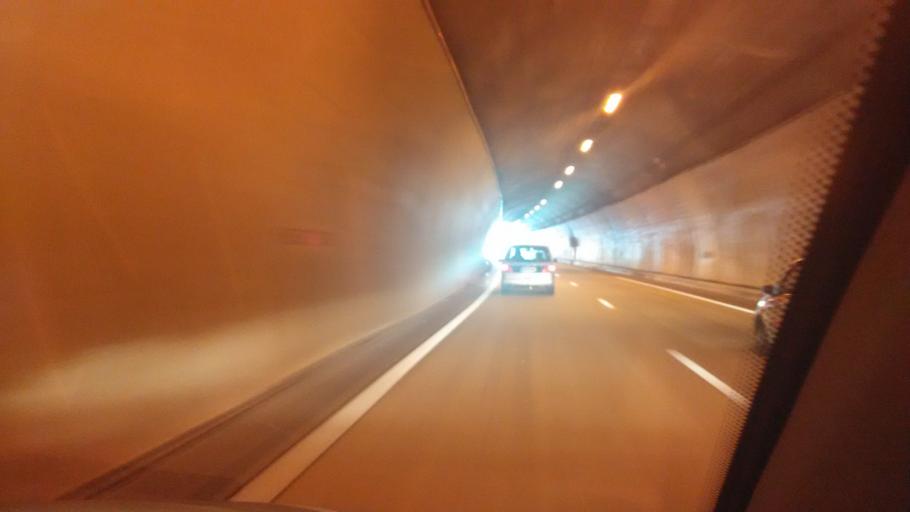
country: FR
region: Provence-Alpes-Cote d'Azur
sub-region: Departement des Alpes-Maritimes
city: Sainte-Agnes
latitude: 43.7856
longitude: 7.4643
